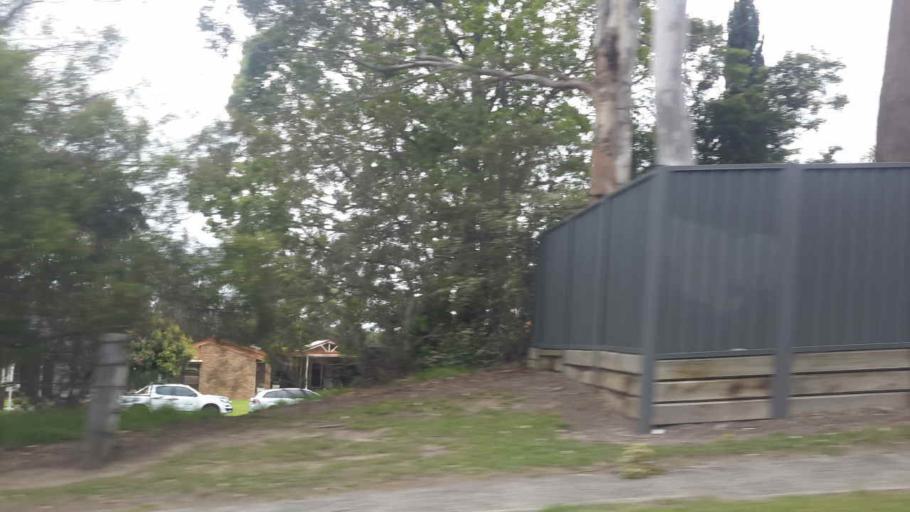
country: AU
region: New South Wales
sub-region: Wollongong
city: Bulli
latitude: -34.3518
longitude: 150.9025
